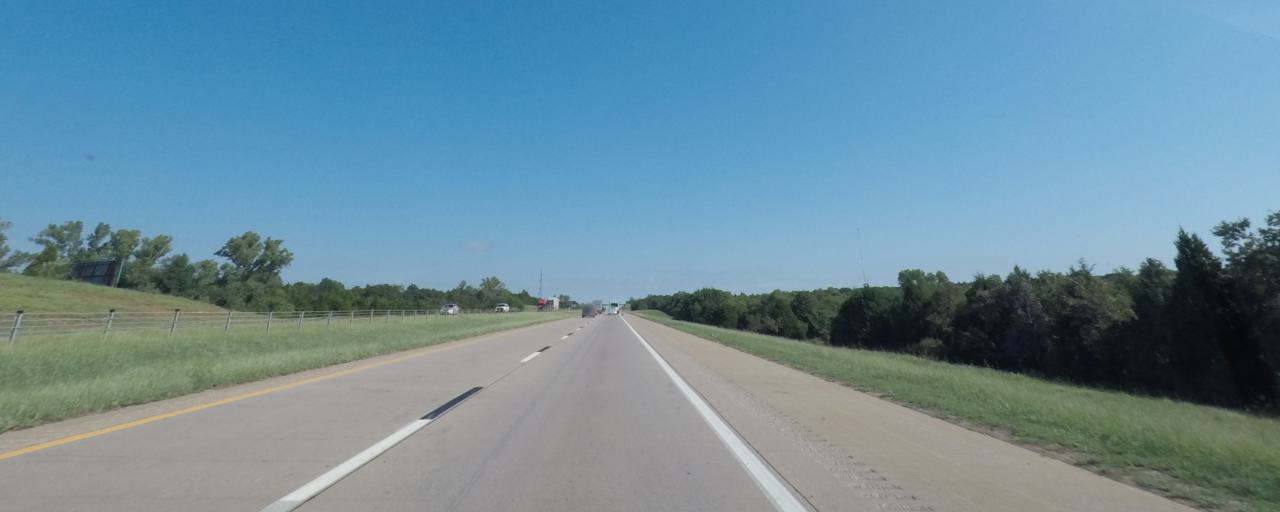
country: US
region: Oklahoma
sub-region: Oklahoma County
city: Edmond
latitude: 35.7457
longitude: -97.4162
